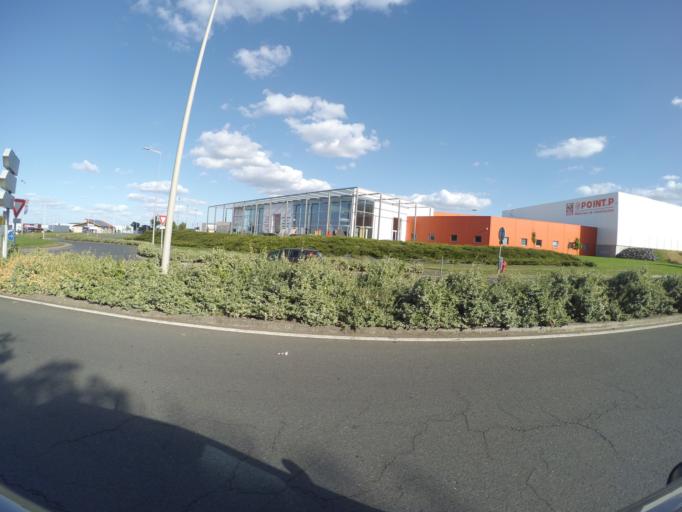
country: FR
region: Pays de la Loire
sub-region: Departement de Maine-et-Loire
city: Mazieres-en-Mauges
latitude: 47.0707
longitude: -0.8418
